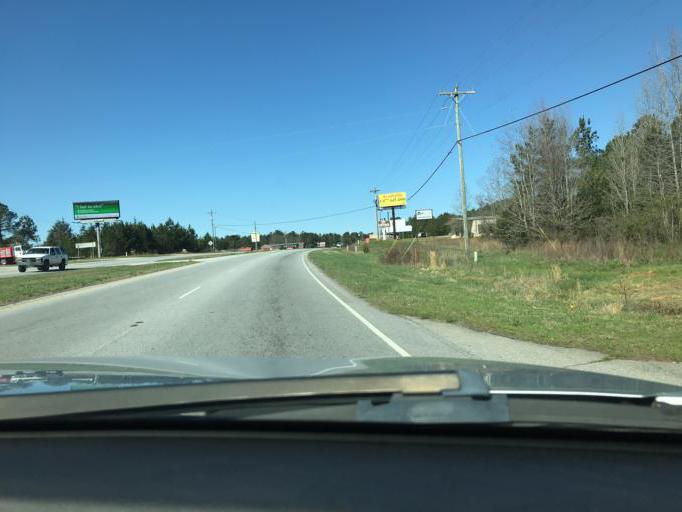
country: US
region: South Carolina
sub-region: Laurens County
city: Watts Mills
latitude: 34.4802
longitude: -81.9453
